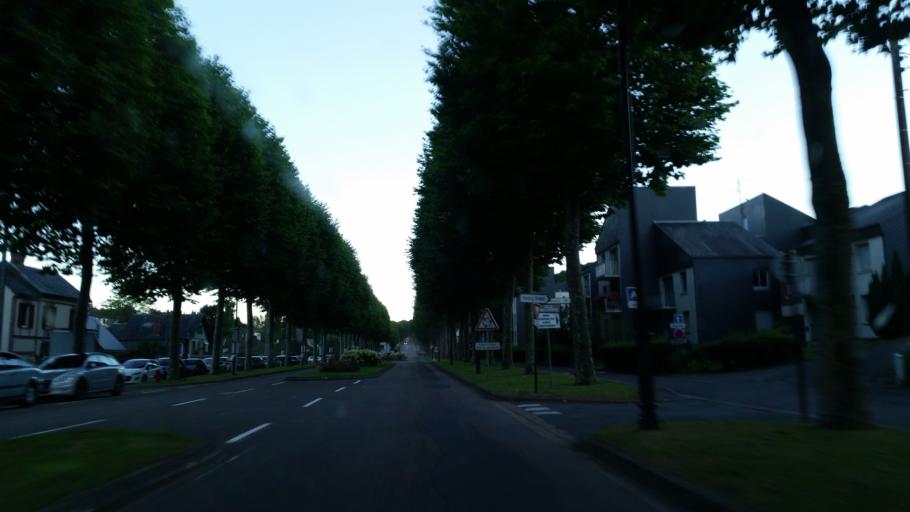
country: FR
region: Lower Normandy
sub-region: Departement du Calvados
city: Honfleur
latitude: 49.4139
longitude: 0.2284
